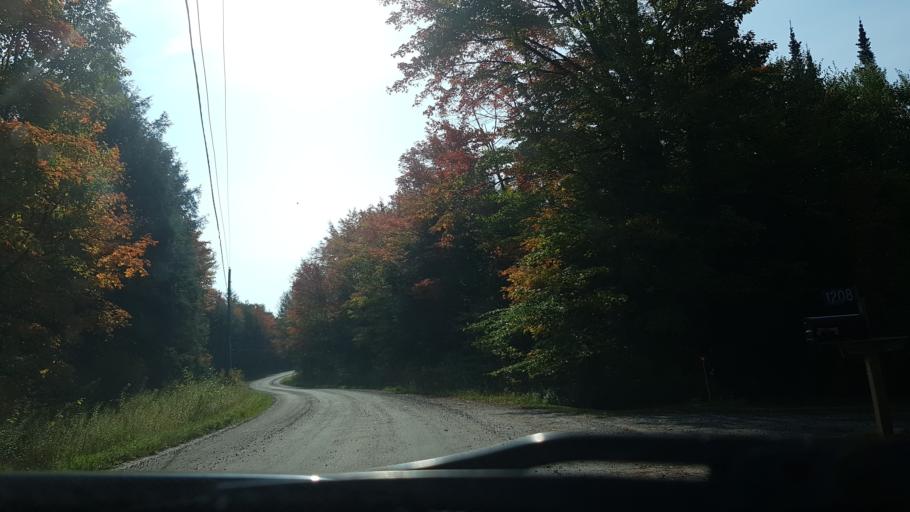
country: CA
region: Ontario
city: Bracebridge
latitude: 44.9327
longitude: -79.2369
